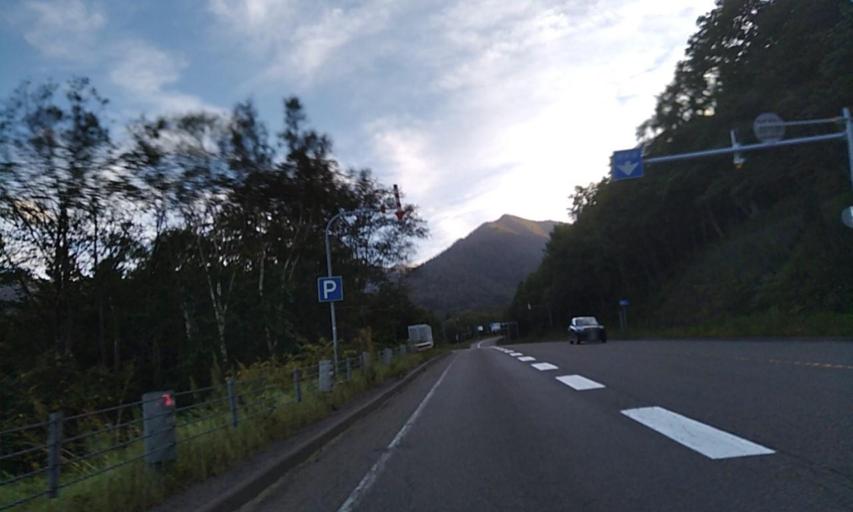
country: JP
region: Hokkaido
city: Otofuke
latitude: 42.9665
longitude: 142.8013
